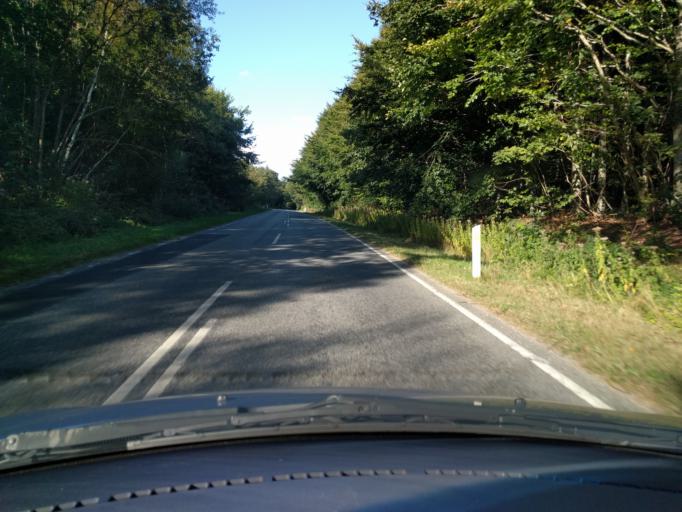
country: DK
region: South Denmark
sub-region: Assens Kommune
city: Assens
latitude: 55.2188
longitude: 9.9973
